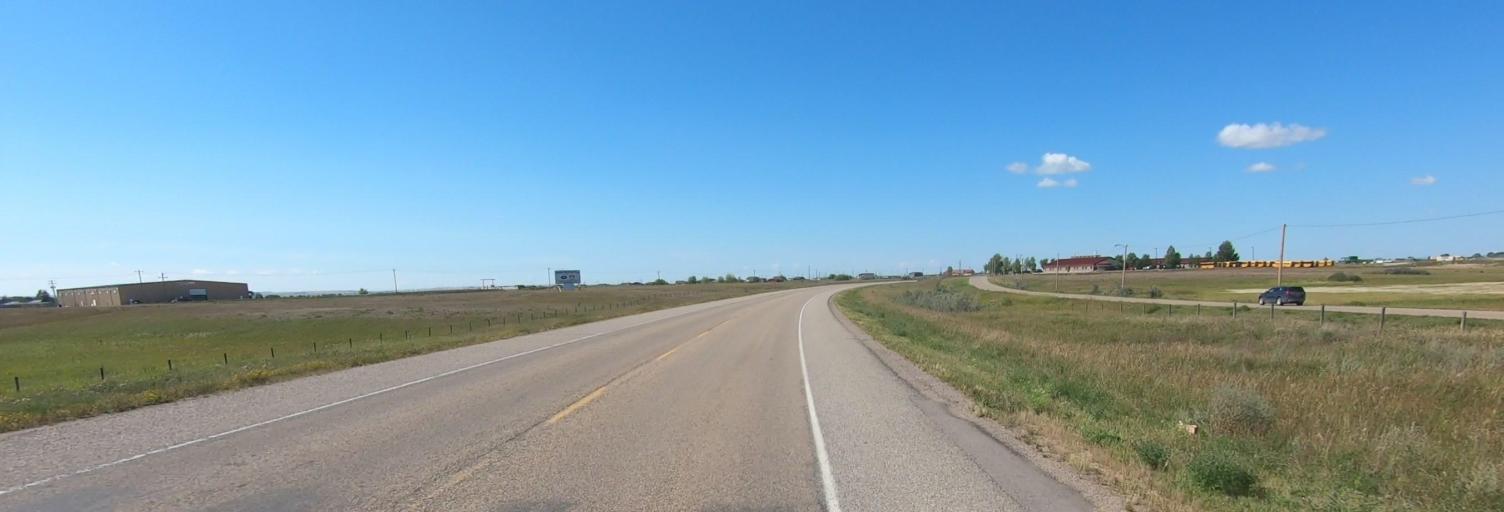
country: CA
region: Alberta
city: Strathmore
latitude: 50.8515
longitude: -113.0235
